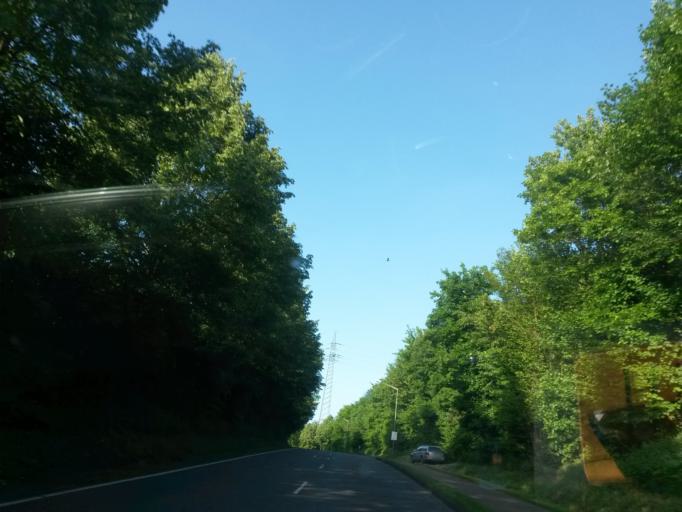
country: DE
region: North Rhine-Westphalia
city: Bergneustadt
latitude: 51.0158
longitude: 7.6529
